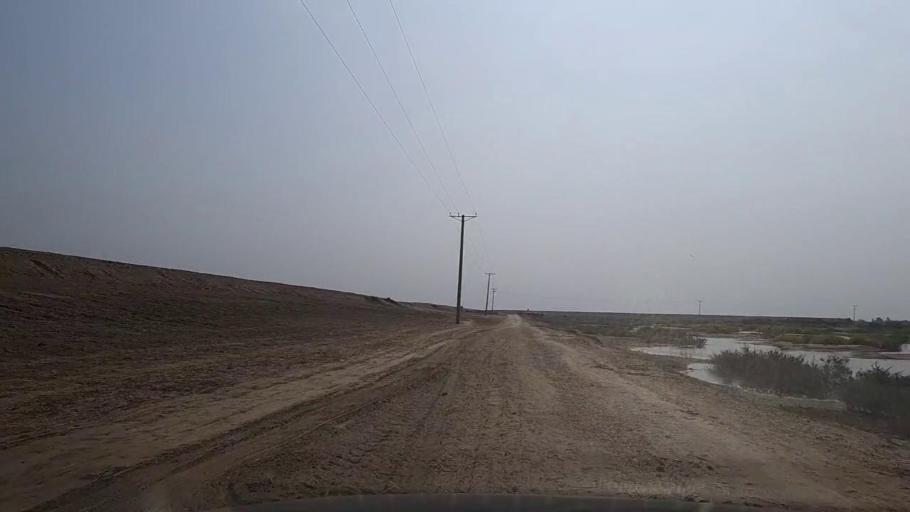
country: PK
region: Sindh
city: Thatta
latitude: 24.5767
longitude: 67.9157
